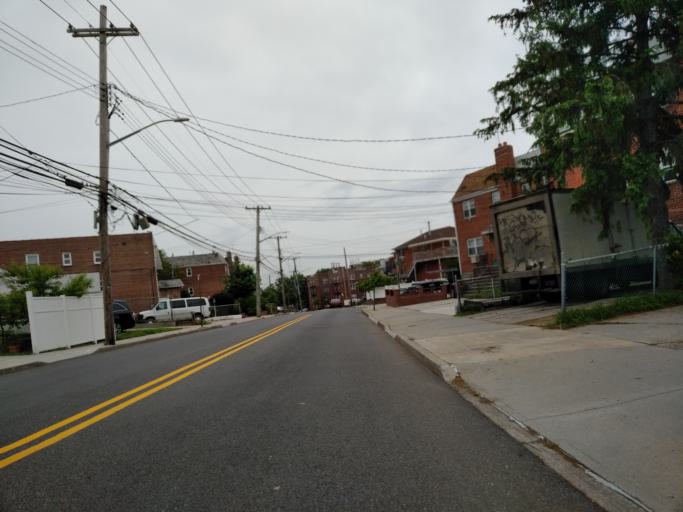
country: US
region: New York
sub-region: Queens County
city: Jamaica
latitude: 40.7475
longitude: -73.8294
